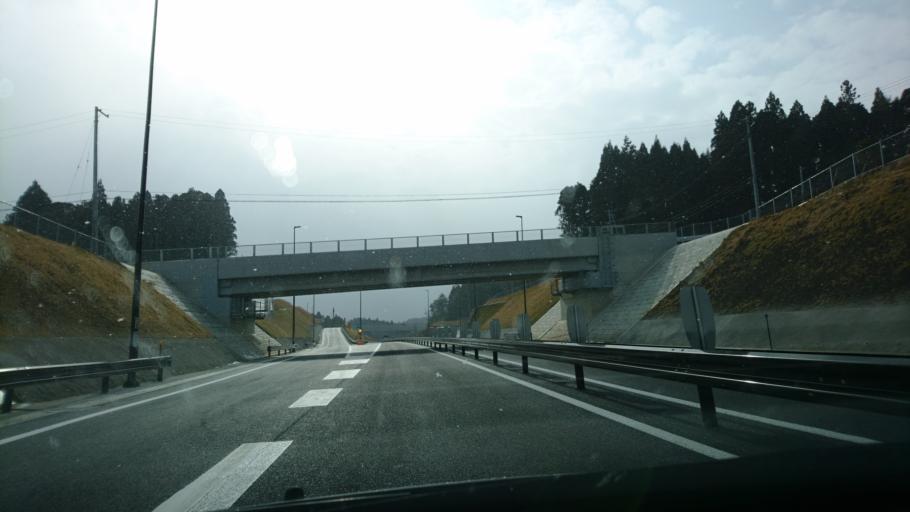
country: JP
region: Iwate
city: Ofunato
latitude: 38.8052
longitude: 141.5405
